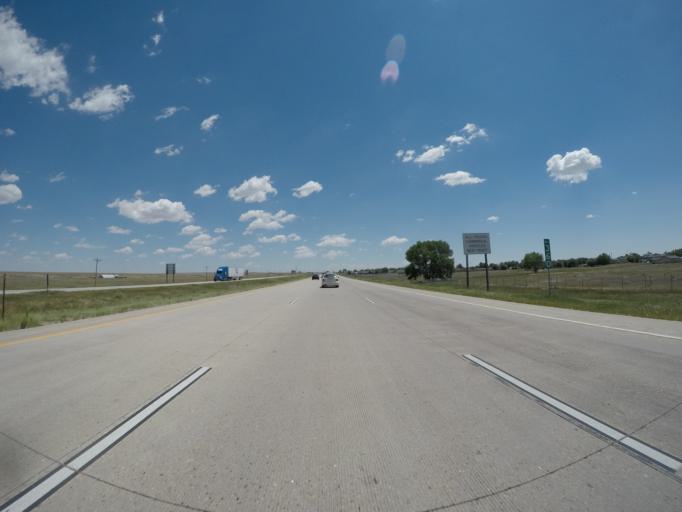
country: US
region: Colorado
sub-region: Lincoln County
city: Limon
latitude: 39.2732
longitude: -103.6980
